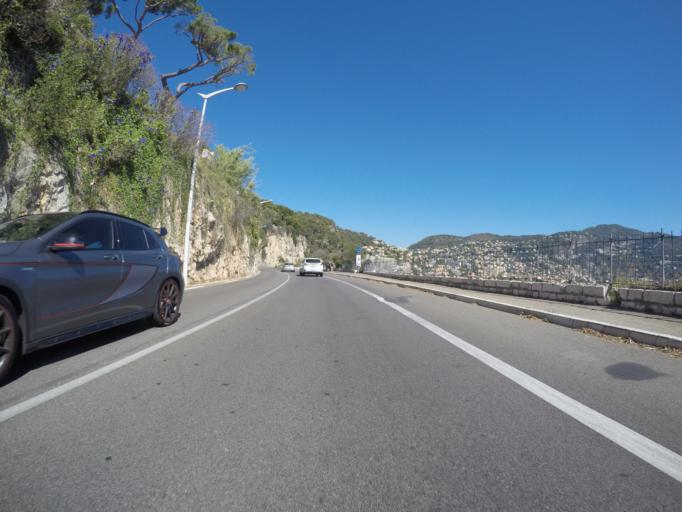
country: FR
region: Provence-Alpes-Cote d'Azur
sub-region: Departement des Alpes-Maritimes
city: Villefranche-sur-Mer
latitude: 43.6935
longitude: 7.3069
